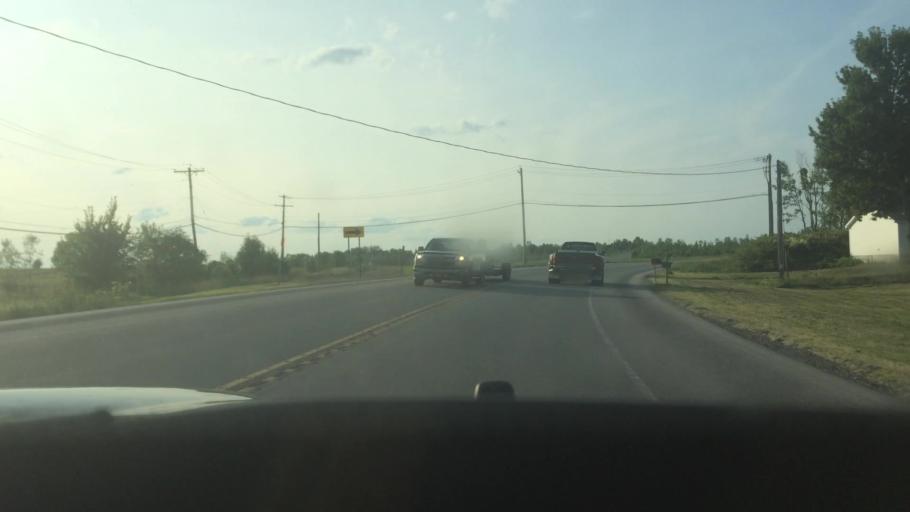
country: US
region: New York
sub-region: St. Lawrence County
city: Ogdensburg
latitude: 44.6822
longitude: -75.4452
